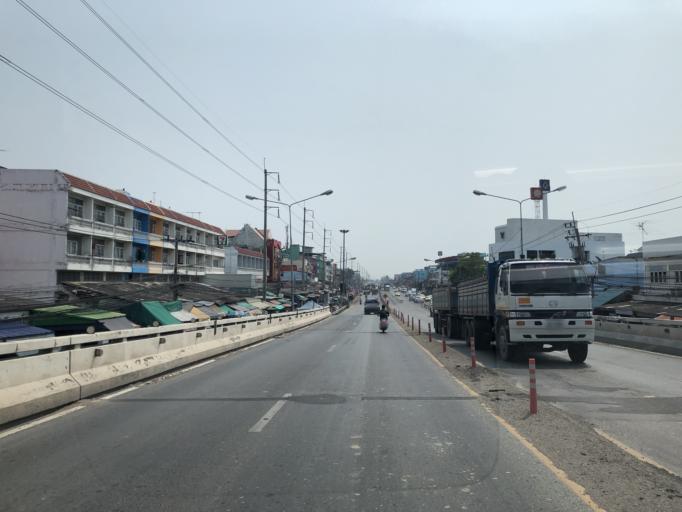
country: TH
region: Samut Prakan
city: Bang Bo
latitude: 13.5088
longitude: 100.8209
